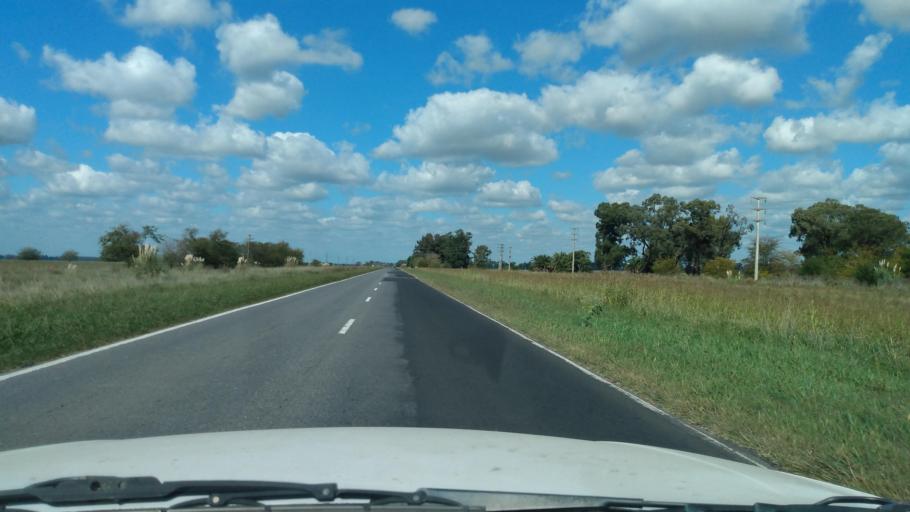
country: AR
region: Buenos Aires
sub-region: Partido de Navarro
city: Navarro
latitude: -34.8999
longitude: -59.3346
